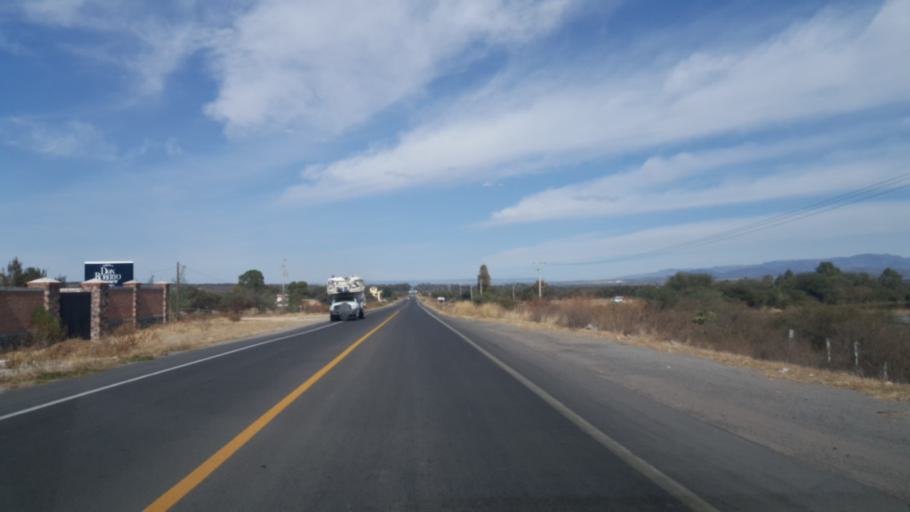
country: MX
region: Jalisco
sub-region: Lagos de Moreno
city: Cristeros [Fraccionamiento]
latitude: 21.2605
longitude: -101.9473
